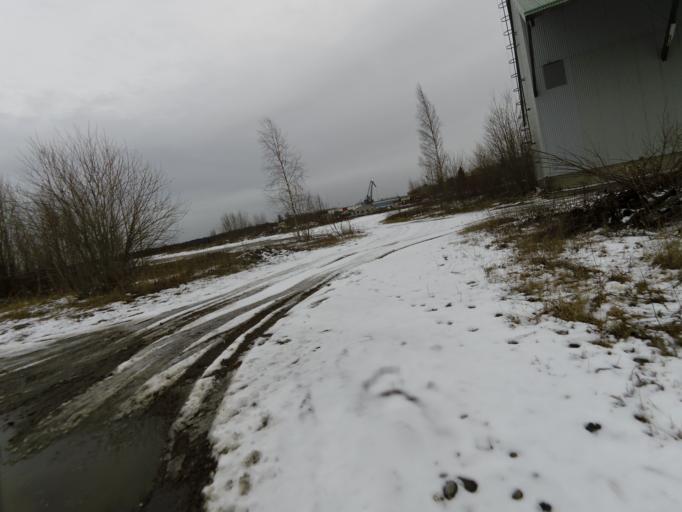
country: SE
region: Gaevleborg
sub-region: Gavle Kommun
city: Gavle
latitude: 60.6814
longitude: 17.1804
